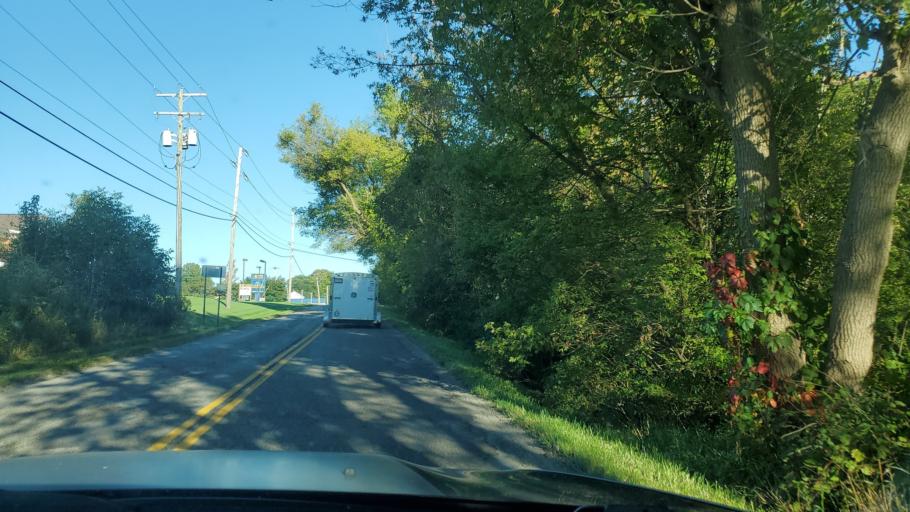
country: US
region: Ohio
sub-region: Mahoning County
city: Boardman
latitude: 40.9879
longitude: -80.6660
